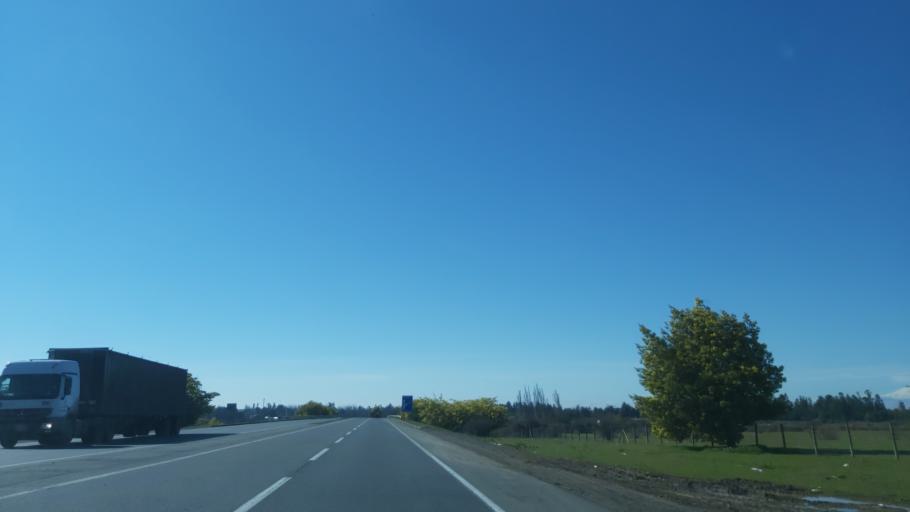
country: CL
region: Biobio
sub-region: Provincia de Nuble
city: Bulnes
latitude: -36.6555
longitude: -72.2429
